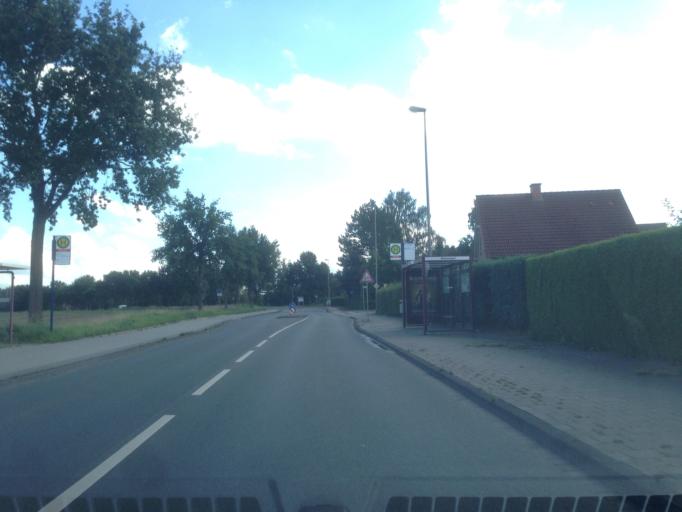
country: DE
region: North Rhine-Westphalia
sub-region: Regierungsbezirk Munster
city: Muenster
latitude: 51.9377
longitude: 7.5739
